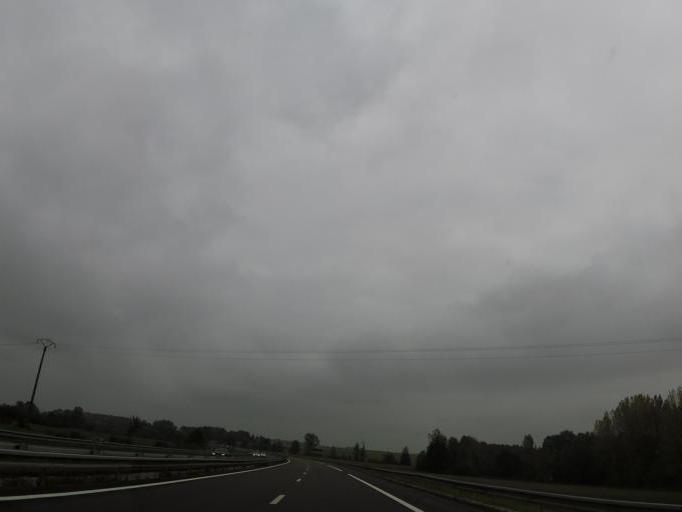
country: FR
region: Champagne-Ardenne
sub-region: Departement de la Marne
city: Sainte-Menehould
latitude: 49.0764
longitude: 4.8340
